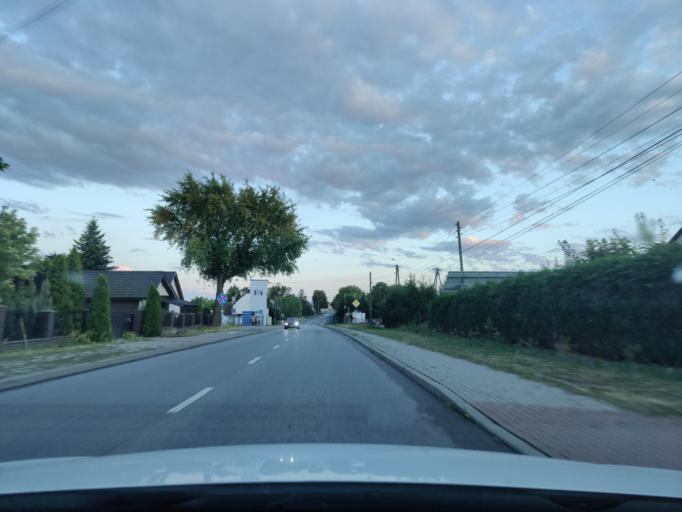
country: PL
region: Opole Voivodeship
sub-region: Powiat nyski
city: Skoroszyce
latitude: 50.5994
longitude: 17.3823
